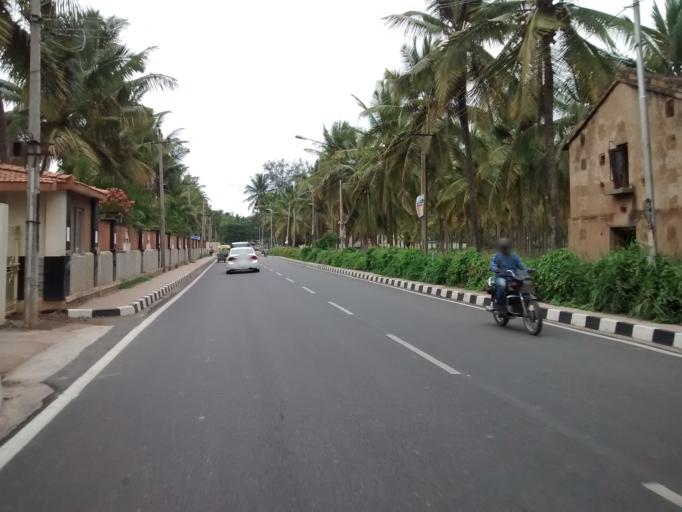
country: IN
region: Karnataka
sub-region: Bangalore Urban
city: Yelahanka
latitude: 13.0417
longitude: 77.5856
